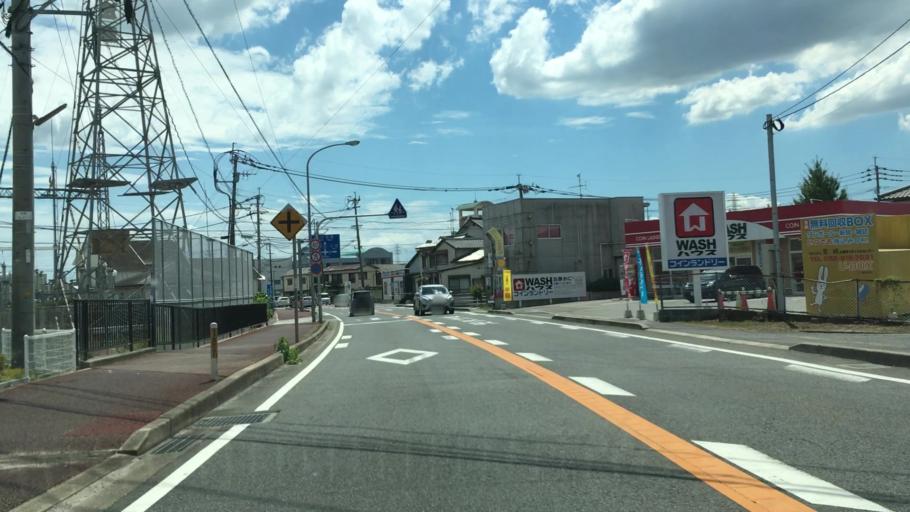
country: JP
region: Saga Prefecture
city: Kanzakimachi-kanzaki
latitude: 33.3097
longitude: 130.3710
